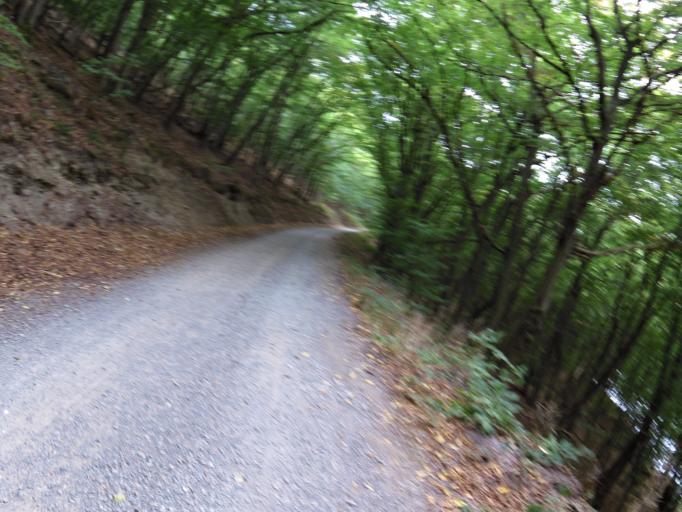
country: DE
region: North Rhine-Westphalia
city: Heimbach
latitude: 50.6085
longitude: 6.4207
